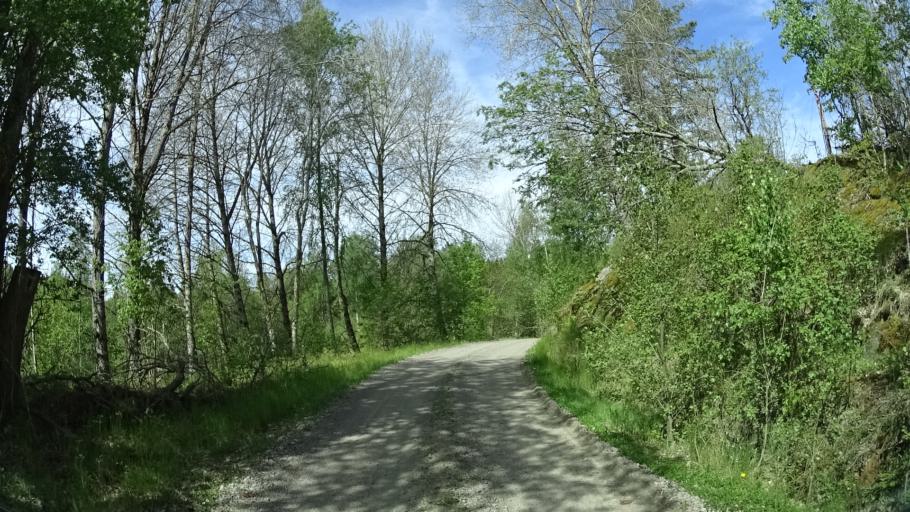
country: SE
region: OEstergoetland
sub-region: Finspangs Kommun
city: Finspang
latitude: 58.7981
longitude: 15.8398
